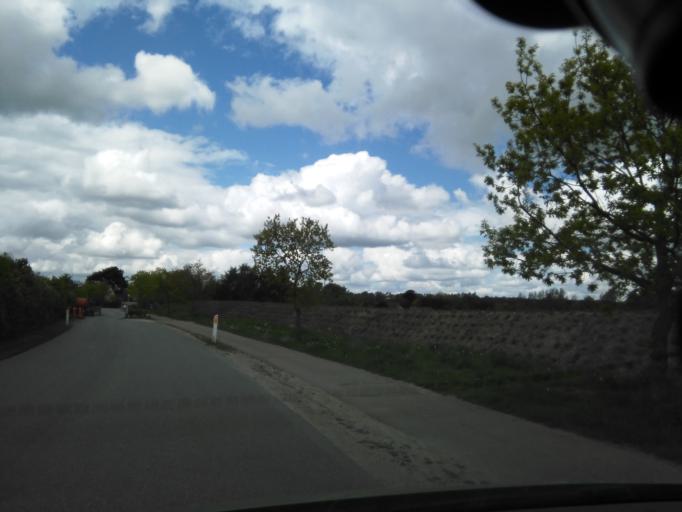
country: DK
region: Central Jutland
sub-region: Skanderborg Kommune
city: Horning
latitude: 56.0791
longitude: 10.0483
